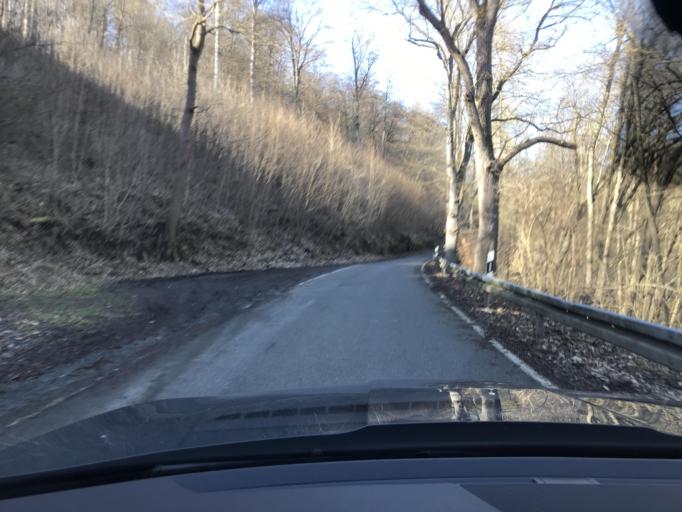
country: DE
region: Saxony-Anhalt
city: Timmenrode
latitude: 51.7202
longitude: 10.9701
